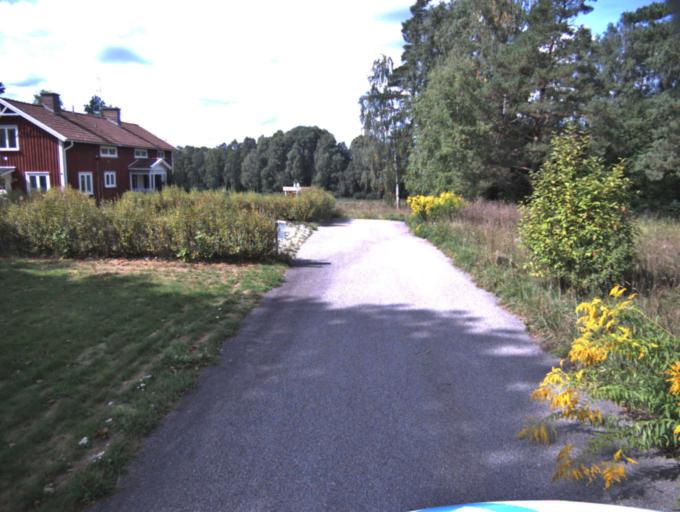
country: SE
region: Vaestra Goetaland
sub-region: Ulricehamns Kommun
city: Ulricehamn
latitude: 57.9345
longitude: 13.4970
